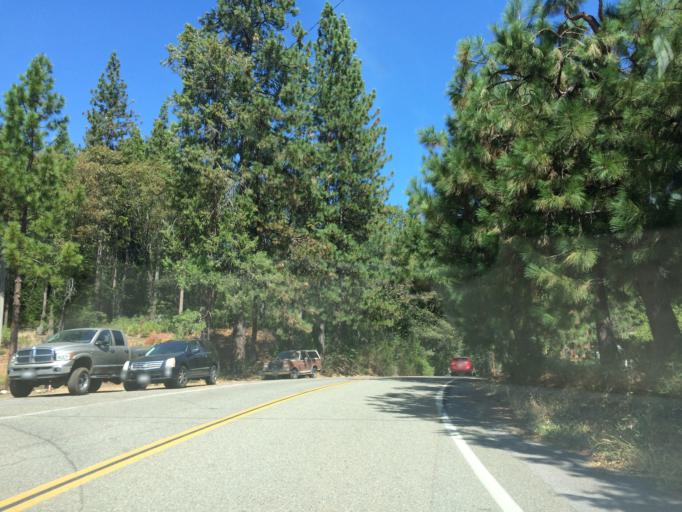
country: US
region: California
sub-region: Siskiyou County
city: Dunsmuir
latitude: 41.1976
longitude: -122.2796
